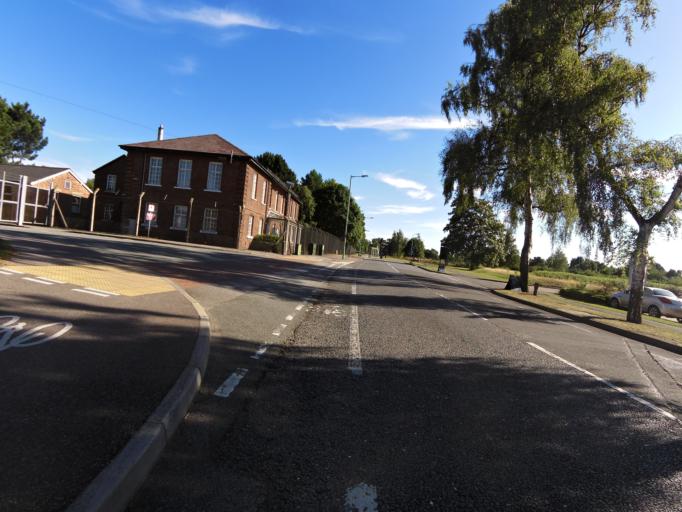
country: GB
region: England
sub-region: Suffolk
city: Kesgrave
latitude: 52.0609
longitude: 1.2785
